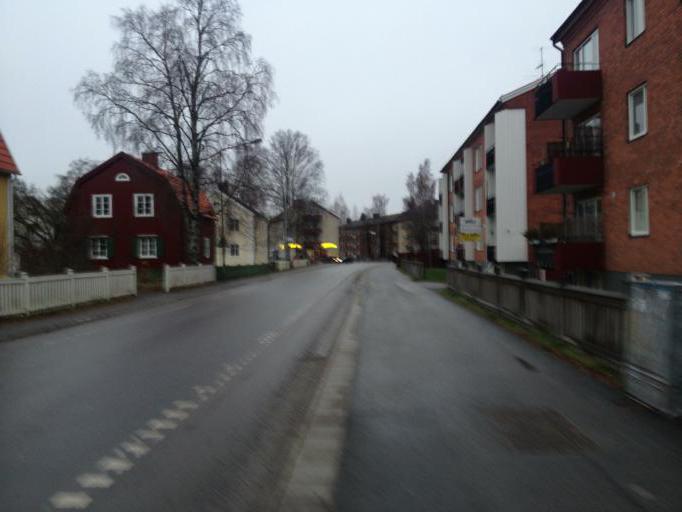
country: SE
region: Vaesterbotten
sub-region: Umea Kommun
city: Umea
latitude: 63.8214
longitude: 20.2862
